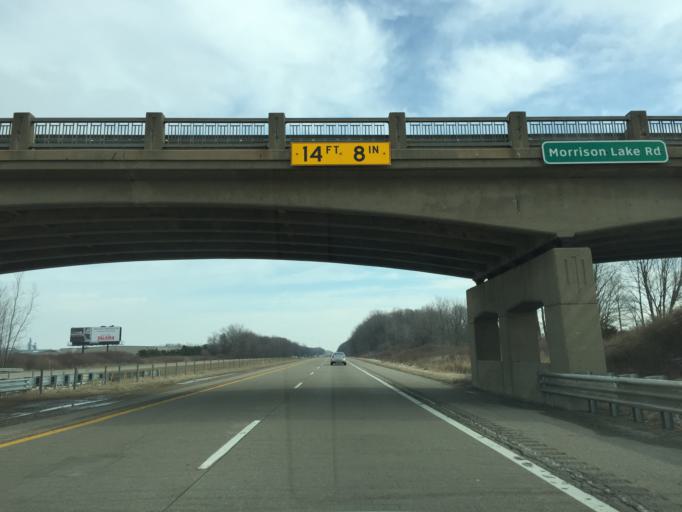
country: US
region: Michigan
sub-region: Ionia County
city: Saranac
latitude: 42.8792
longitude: -85.2139
